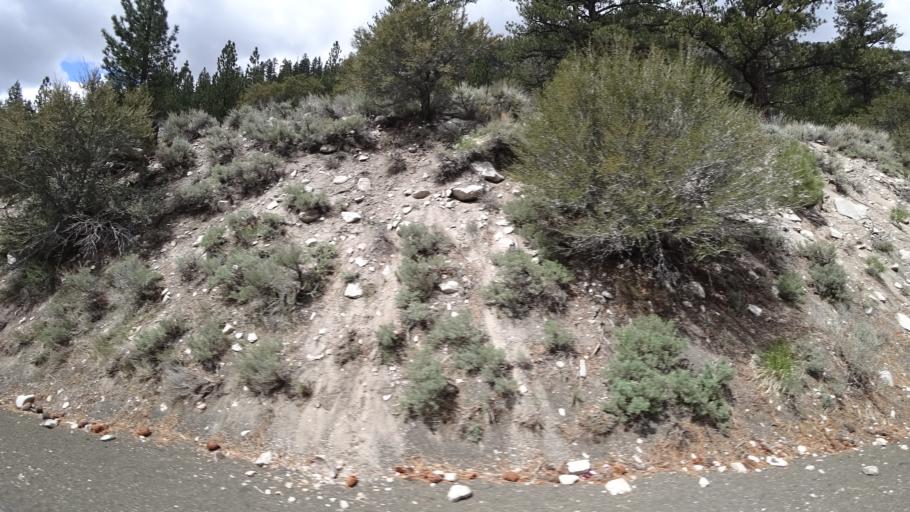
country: US
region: California
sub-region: Mono County
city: Bridgeport
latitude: 38.3983
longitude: -119.4529
